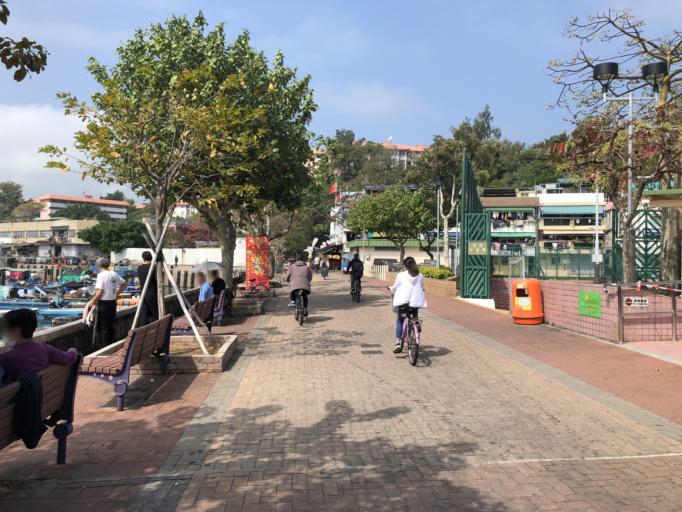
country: HK
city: Yung Shue Wan
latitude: 22.2115
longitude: 114.0269
